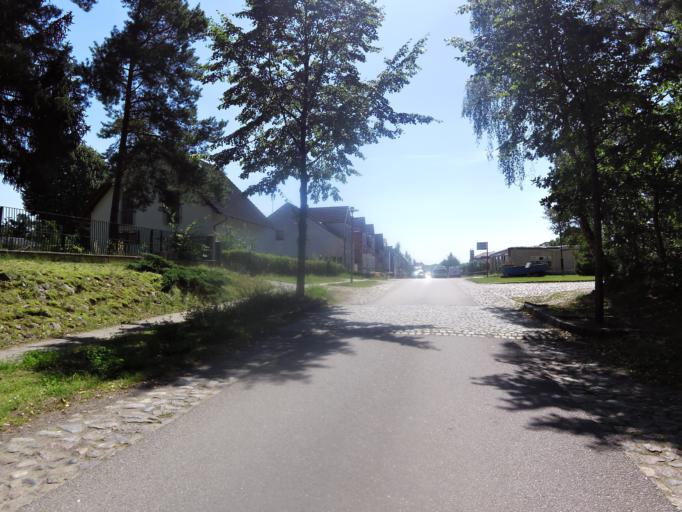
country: DE
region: Brandenburg
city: Furstenberg
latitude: 53.1806
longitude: 13.2264
